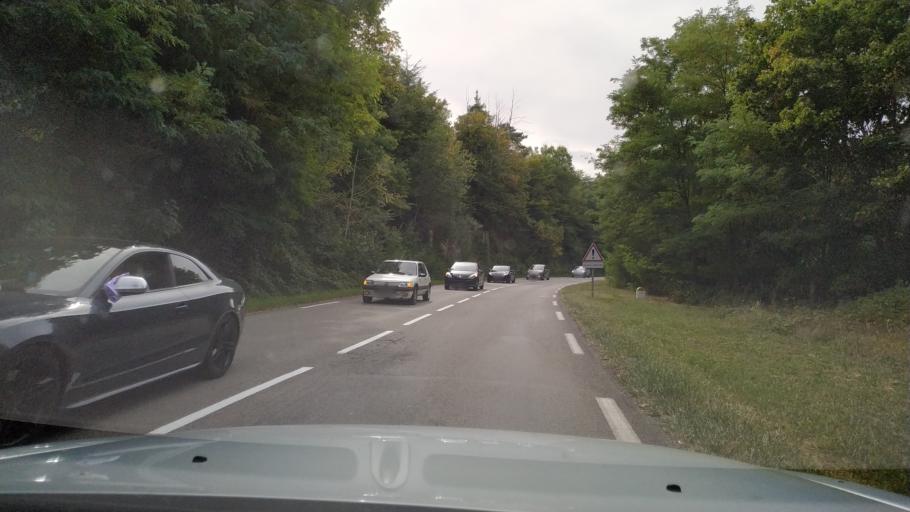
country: FR
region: Rhone-Alpes
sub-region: Departement de l'Ardeche
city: Lamastre
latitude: 44.9858
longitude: 4.5484
